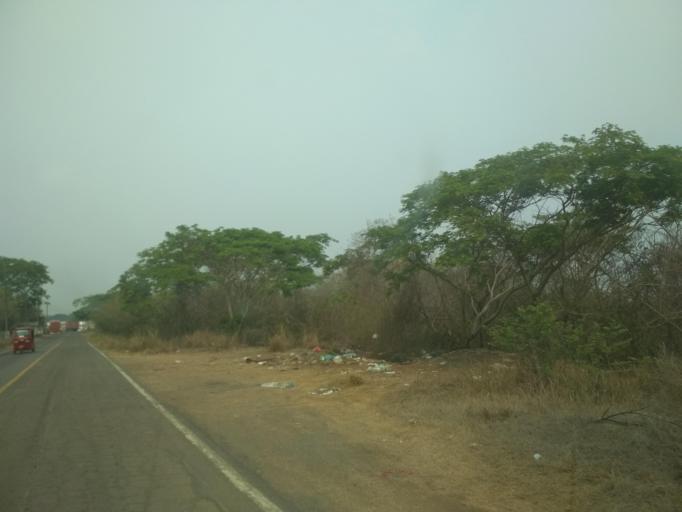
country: MX
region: Veracruz
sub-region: Veracruz
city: Delfino Victoria (Santa Fe)
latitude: 19.2185
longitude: -96.2579
